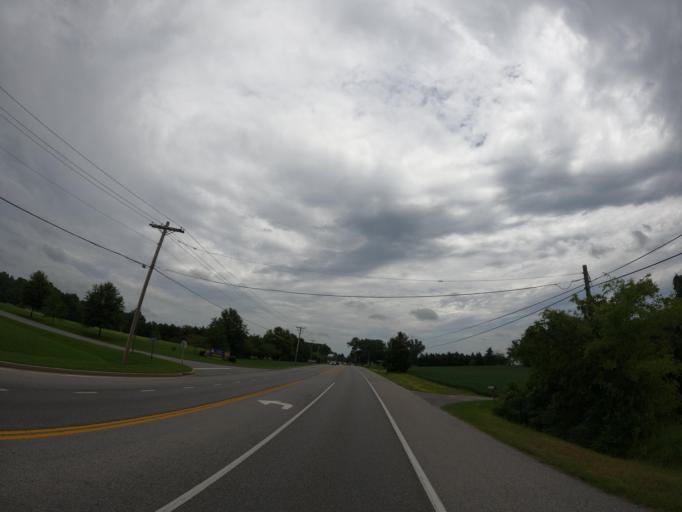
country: US
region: Maryland
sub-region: Saint Mary's County
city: California
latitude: 38.2383
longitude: -76.5160
